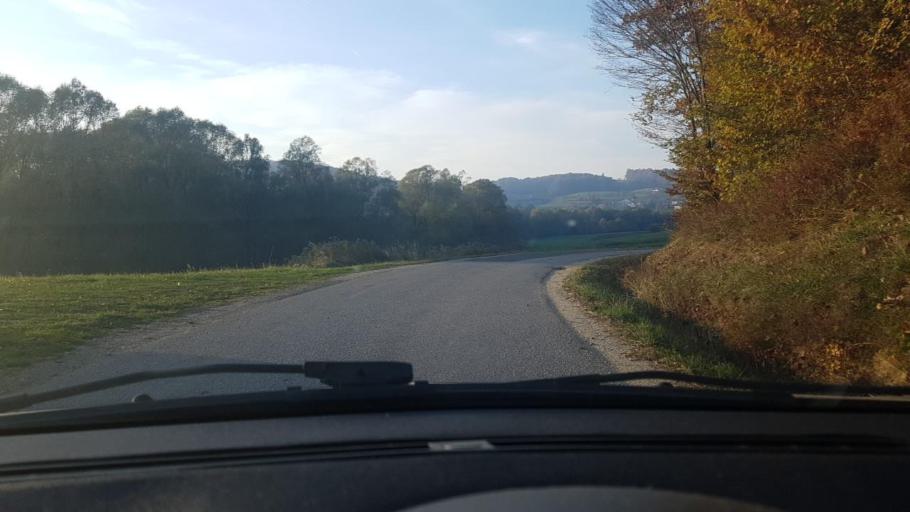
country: SI
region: Rogaska Slatina
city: Rogaska Slatina
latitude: 46.2056
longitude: 15.6481
